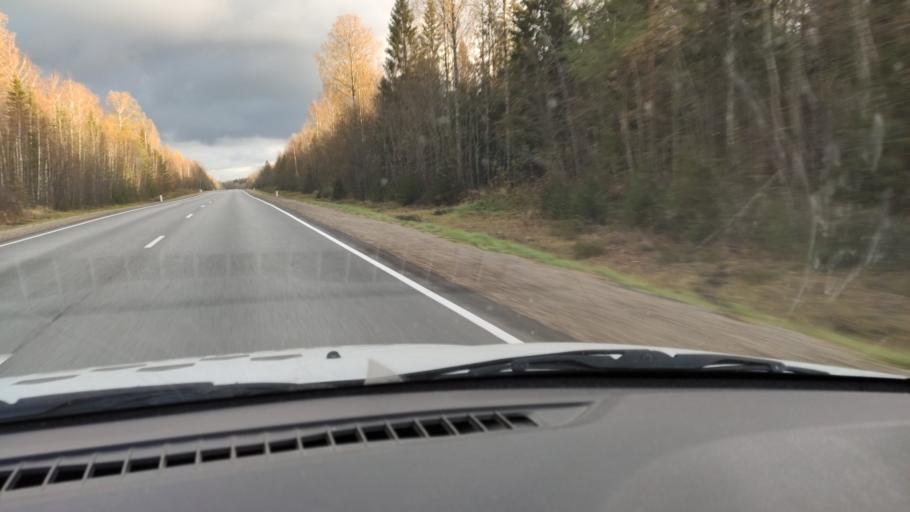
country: RU
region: Kirov
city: Chernaya Kholunitsa
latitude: 58.7847
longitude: 51.9036
